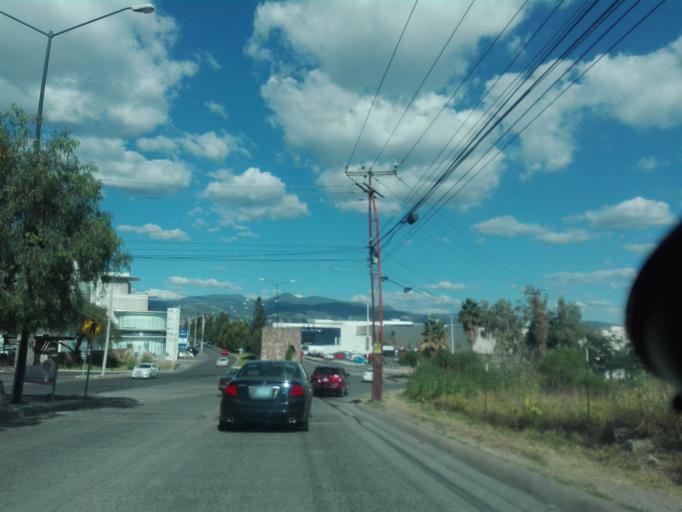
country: MX
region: Guanajuato
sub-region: Leon
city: La Ermita
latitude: 21.1582
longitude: -101.6998
